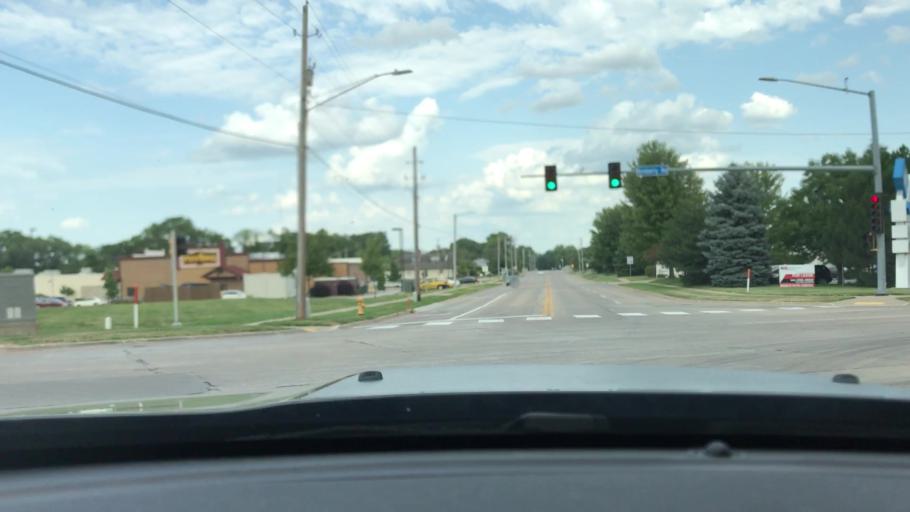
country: US
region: Iowa
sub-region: Scott County
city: Bettendorf
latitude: 41.5367
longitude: -90.5217
